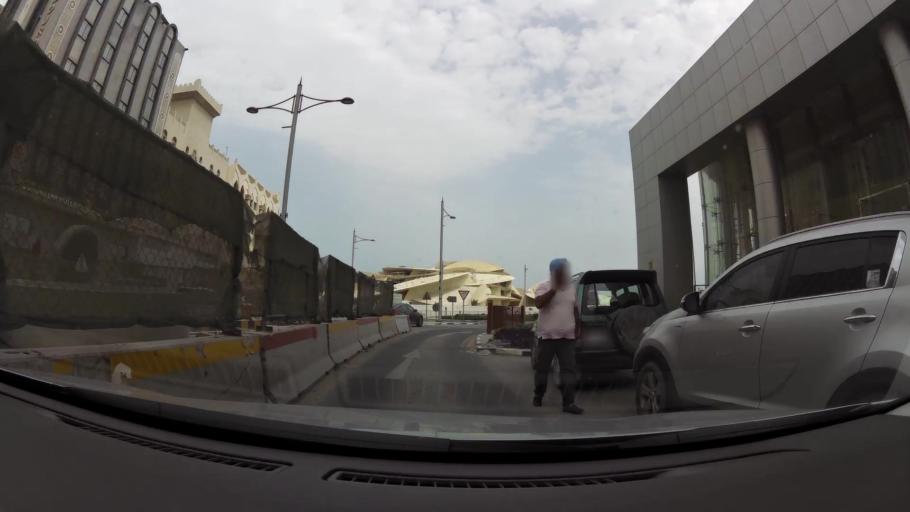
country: QA
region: Baladiyat ad Dawhah
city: Doha
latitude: 25.2869
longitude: 51.5471
